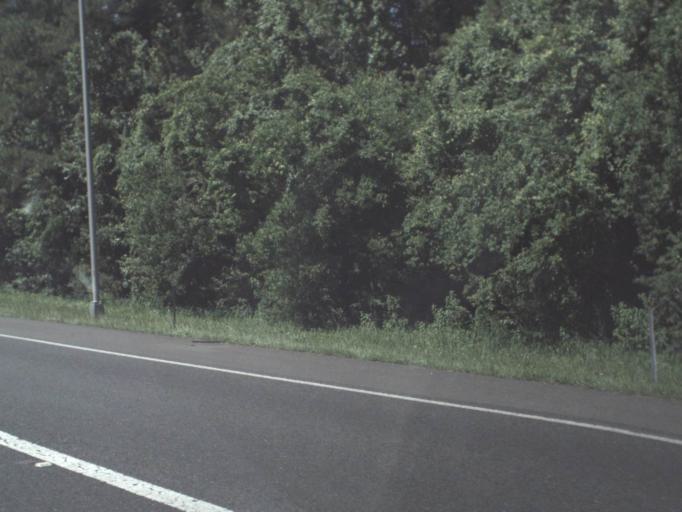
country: US
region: Florida
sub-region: Duval County
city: Jacksonville
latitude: 30.3099
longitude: -81.7705
